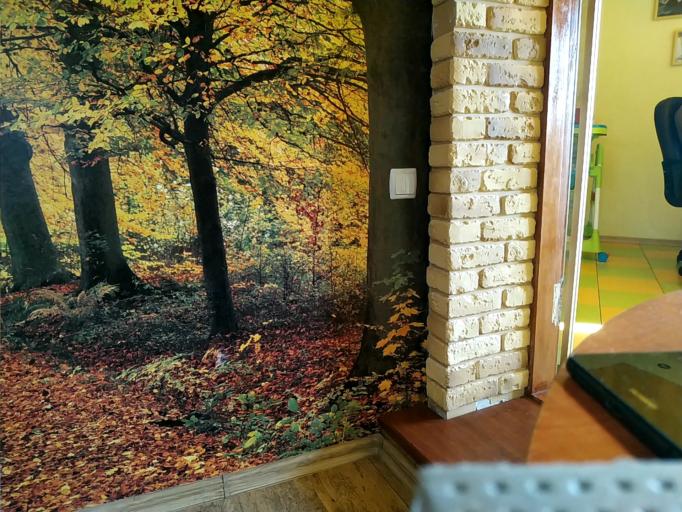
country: RU
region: Tverskaya
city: Zubtsov
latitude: 56.2022
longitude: 34.5676
